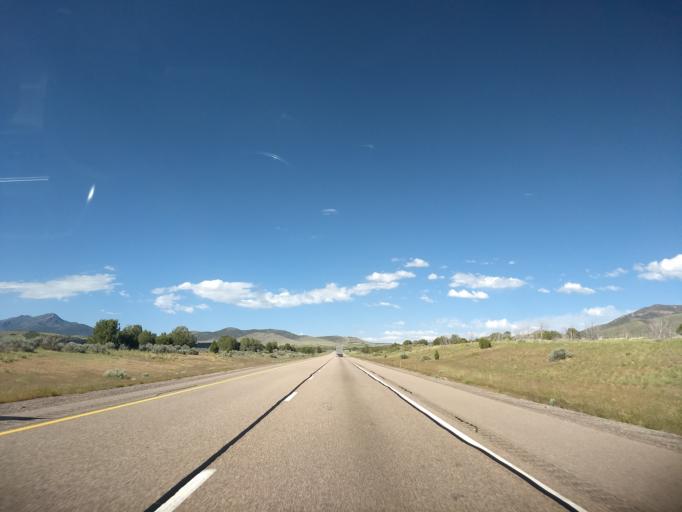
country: US
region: Utah
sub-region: Millard County
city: Fillmore
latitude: 39.1602
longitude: -112.2230
